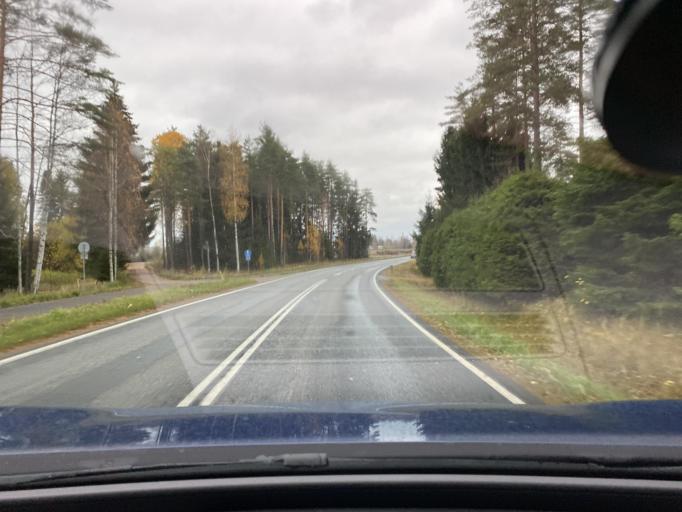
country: FI
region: Satakunta
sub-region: Rauma
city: Saekylae
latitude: 61.0615
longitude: 22.4913
